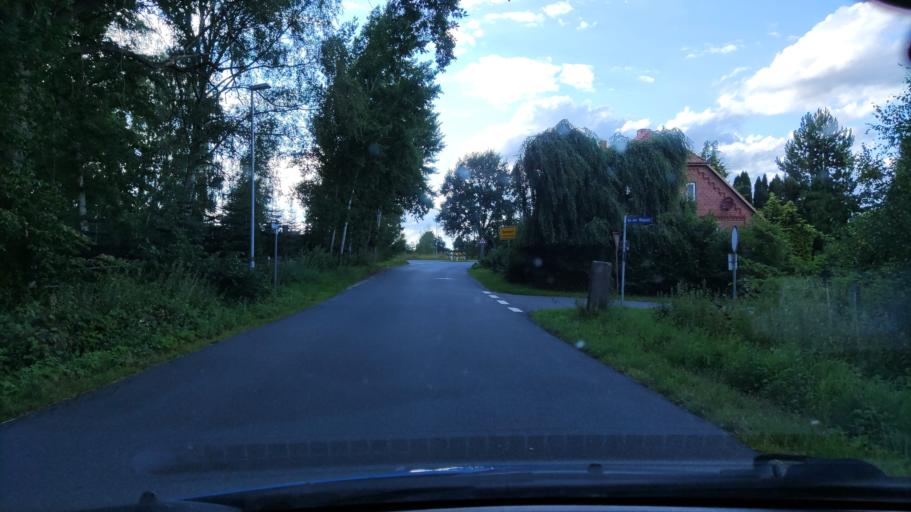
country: DE
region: Lower Saxony
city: Dahlenburg
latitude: 53.1777
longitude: 10.6967
